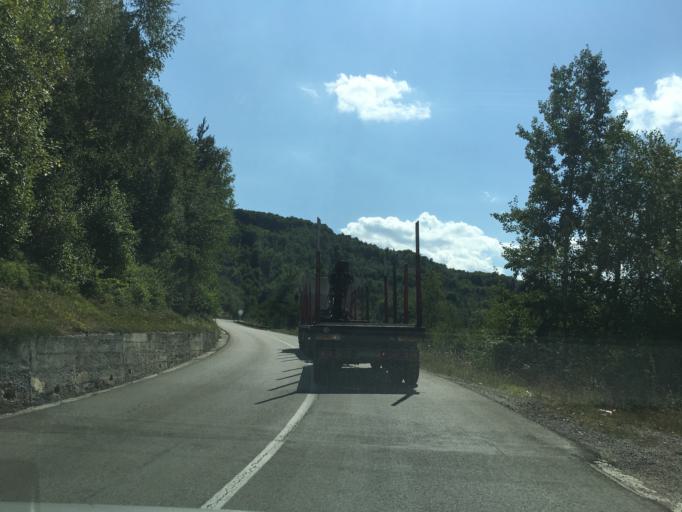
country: RS
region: Central Serbia
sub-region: Zlatiborski Okrug
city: Prijepolje
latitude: 43.3458
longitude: 19.5714
